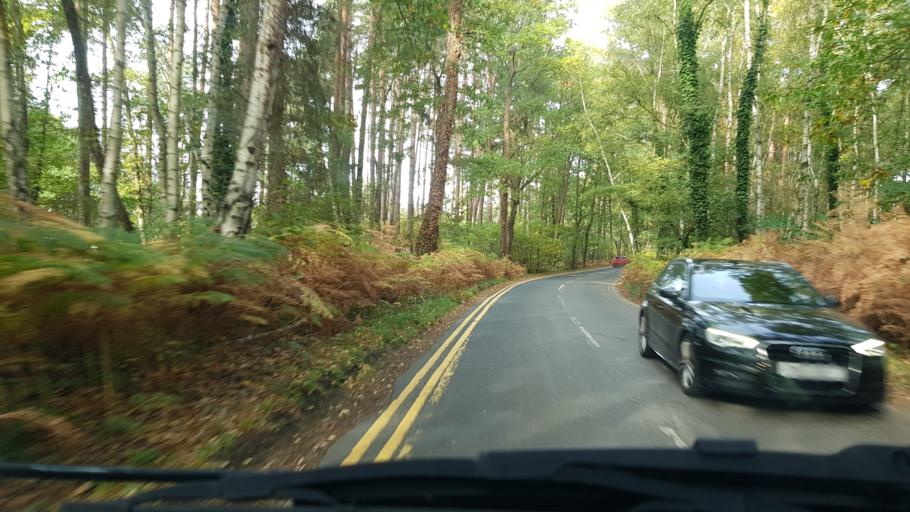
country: GB
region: England
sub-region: Surrey
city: Ripley
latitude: 51.3131
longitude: -0.4689
